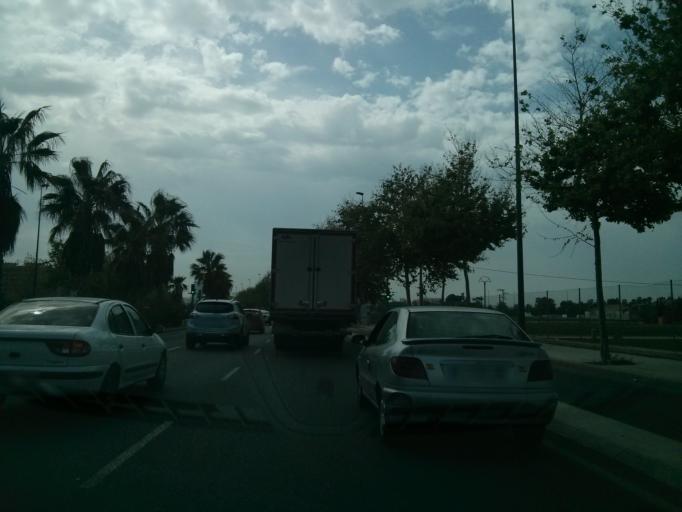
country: ES
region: Valencia
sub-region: Provincia de Valencia
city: Tavernes Blanques
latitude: 39.4994
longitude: -0.3773
